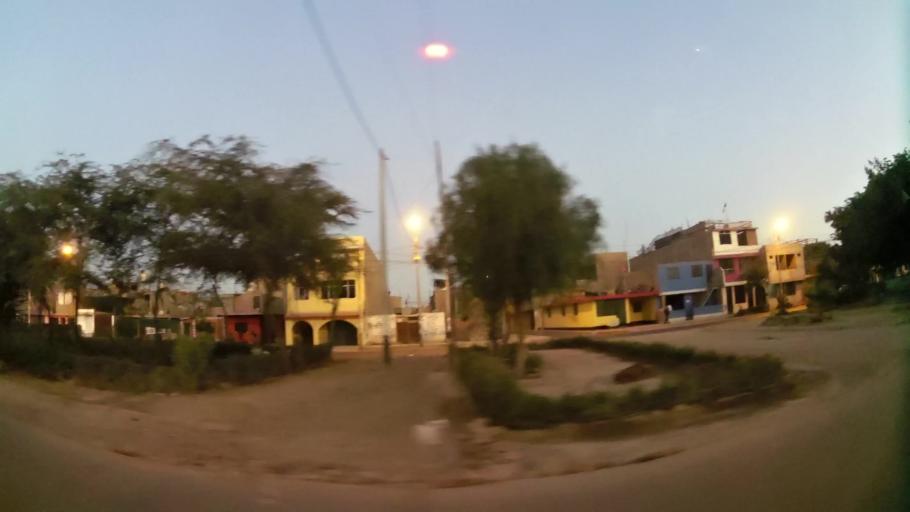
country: PE
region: Ica
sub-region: Provincia de Ica
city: Ica
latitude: -14.0789
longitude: -75.7340
